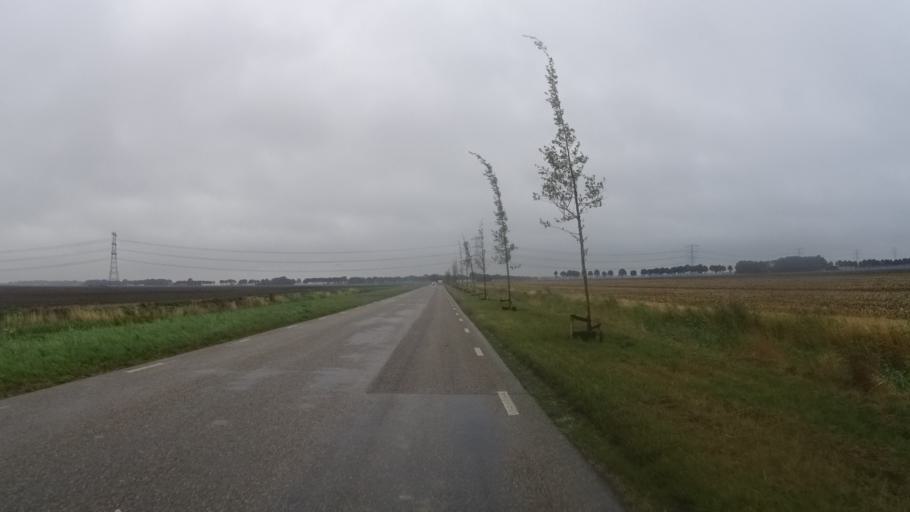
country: NL
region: Groningen
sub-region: Gemeente Veendam
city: Veendam
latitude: 53.1918
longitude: 6.9070
